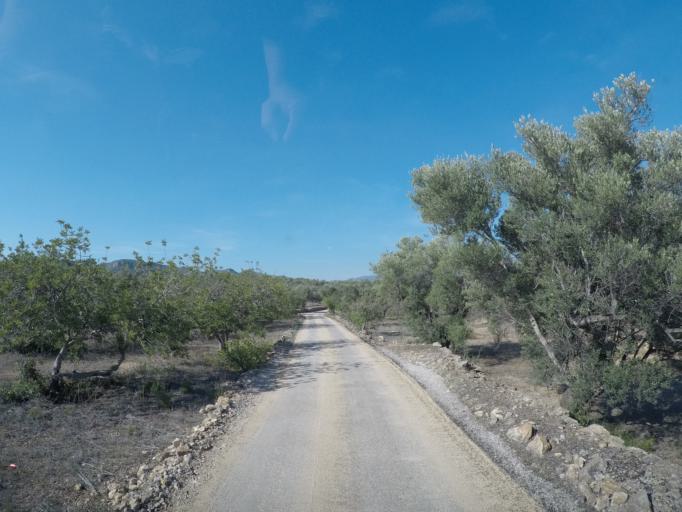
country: ES
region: Catalonia
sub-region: Provincia de Tarragona
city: El Perello
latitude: 40.9065
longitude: 0.7270
